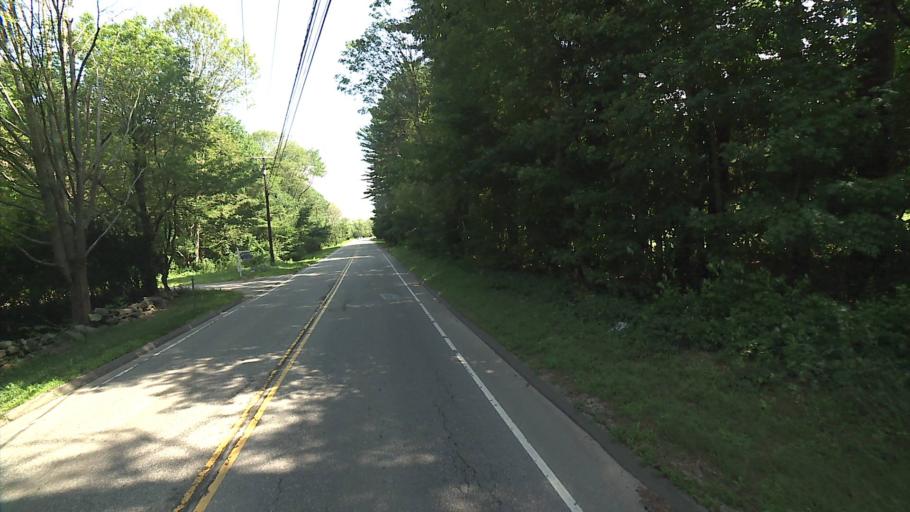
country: US
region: Connecticut
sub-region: Middlesex County
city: Westbrook Center
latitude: 41.3139
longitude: -72.4342
